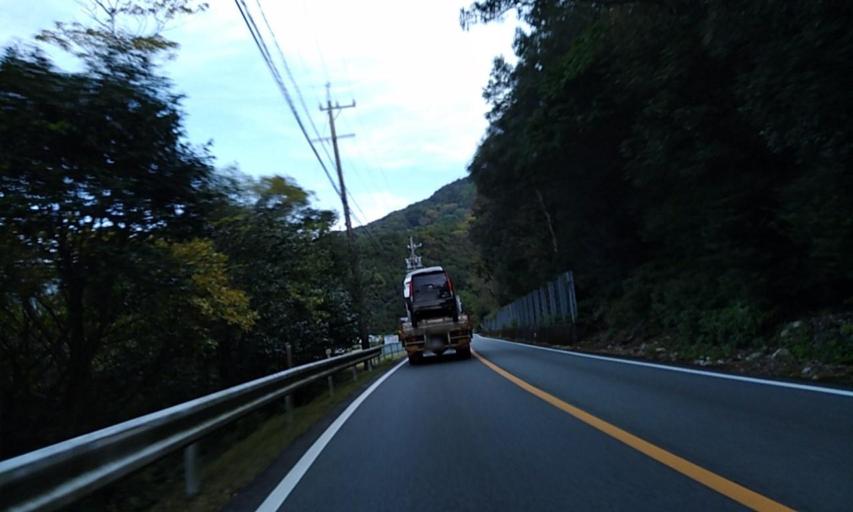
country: JP
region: Mie
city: Toba
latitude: 34.3989
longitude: 136.7833
